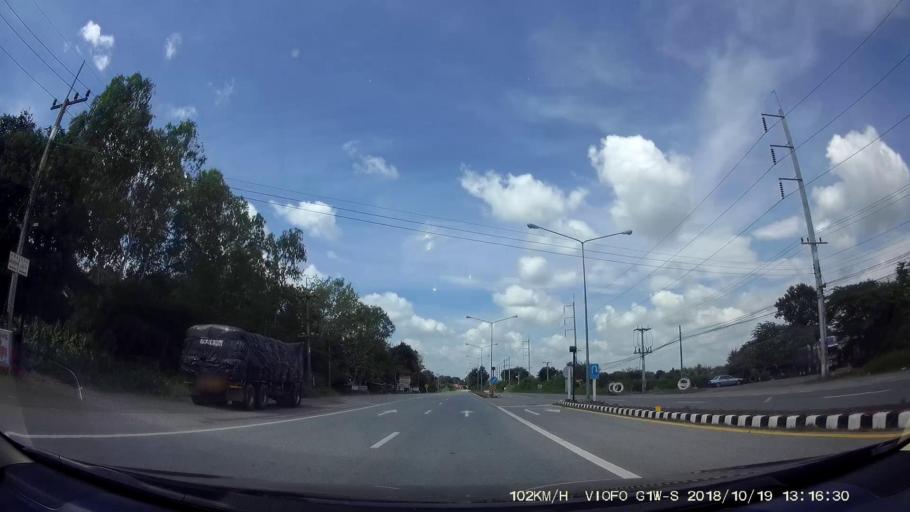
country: TH
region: Chaiyaphum
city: Chatturat
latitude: 15.4047
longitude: 101.8357
